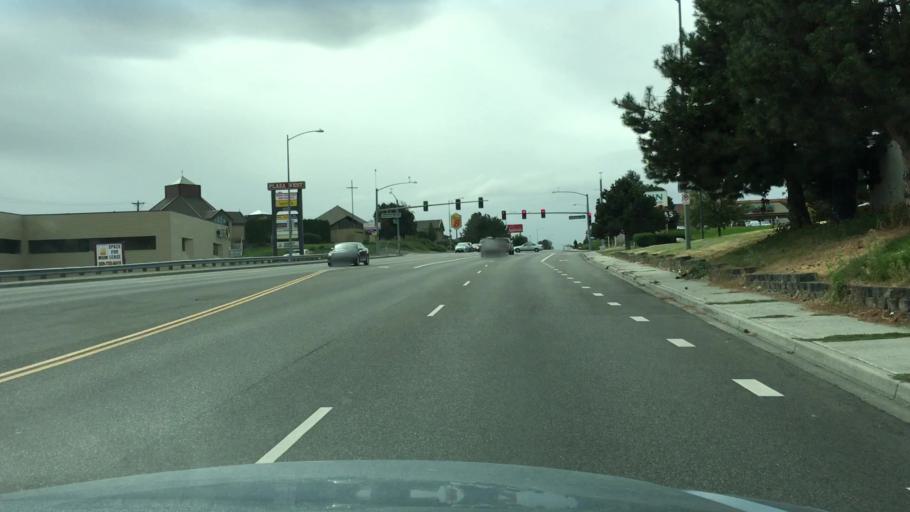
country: US
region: Washington
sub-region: Franklin County
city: West Pasco
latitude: 46.2194
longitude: -119.2243
